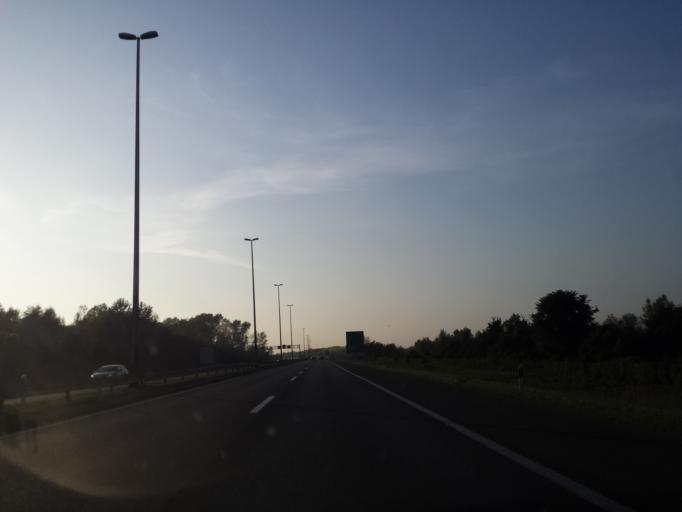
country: HR
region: Grad Zagreb
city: Jezdovec
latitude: 45.7812
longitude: 15.8671
